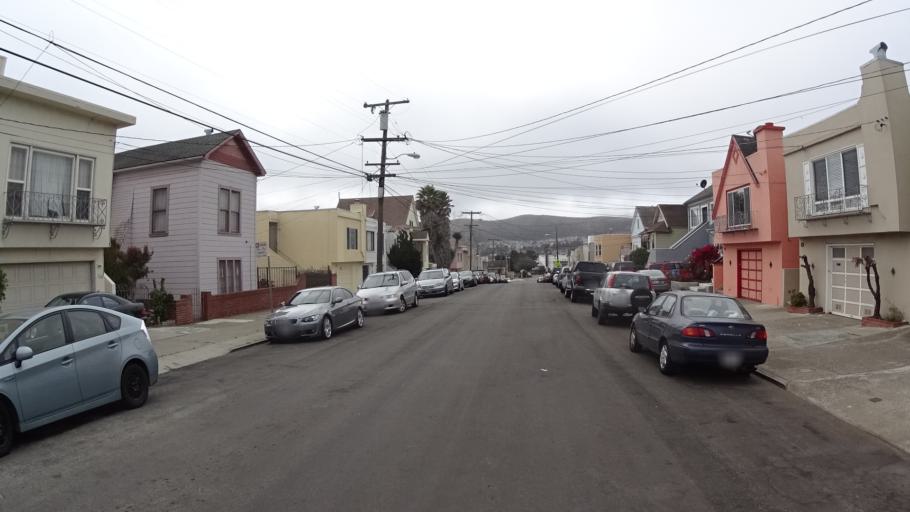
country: US
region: California
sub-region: San Mateo County
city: Brisbane
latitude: 37.7116
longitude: -122.4089
